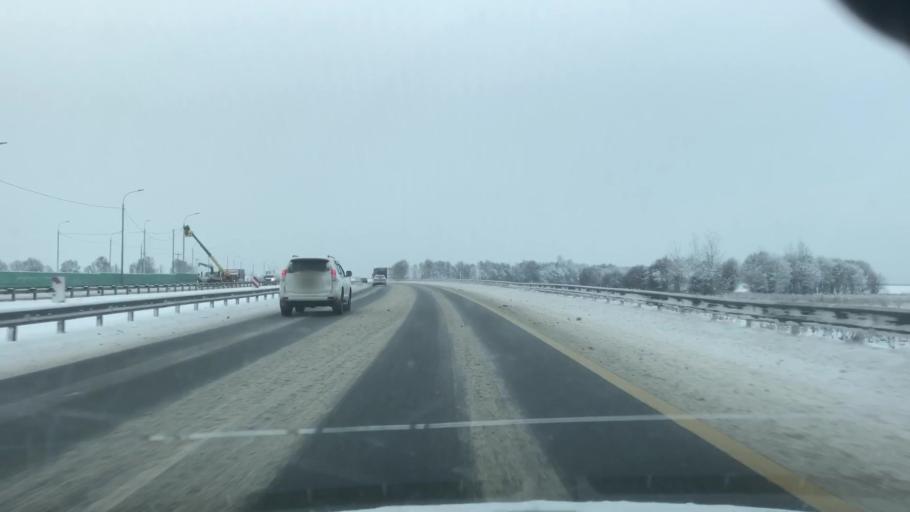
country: RU
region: Moskovskaya
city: Mikhnevo
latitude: 55.1162
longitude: 37.9267
